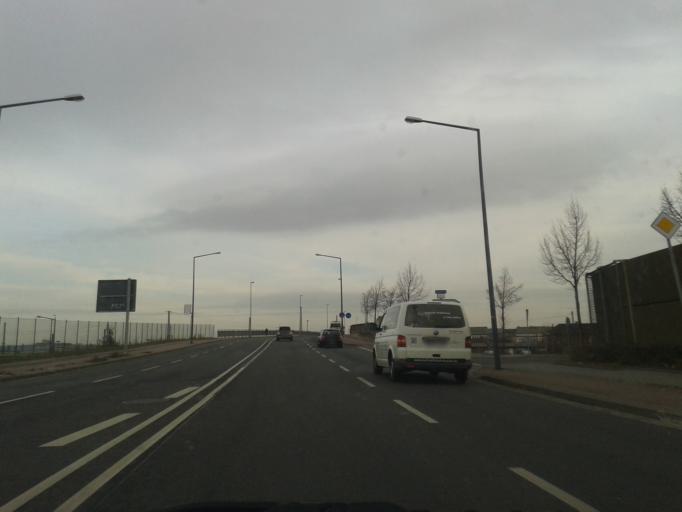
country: DE
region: Saxony
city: Dresden
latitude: 51.0525
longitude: 13.7075
